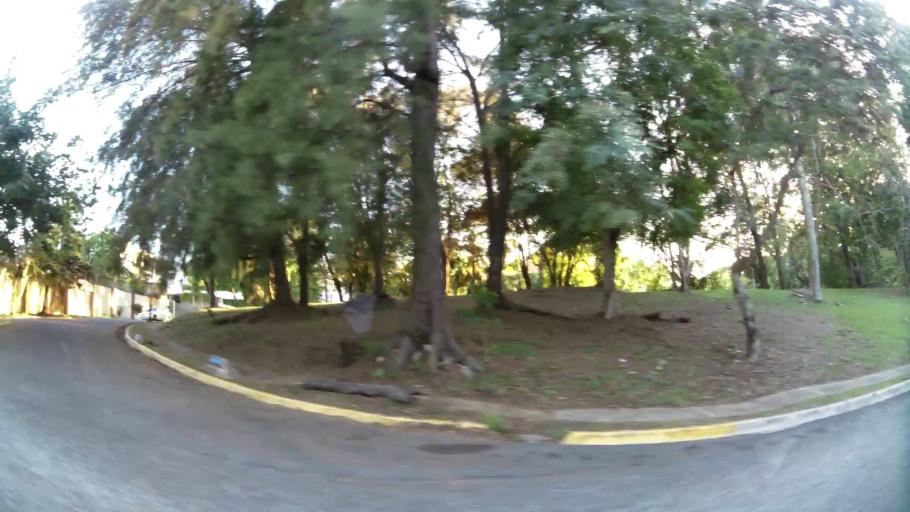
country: DO
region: Nacional
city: Santo Domingo
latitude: 18.4902
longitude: -69.9619
